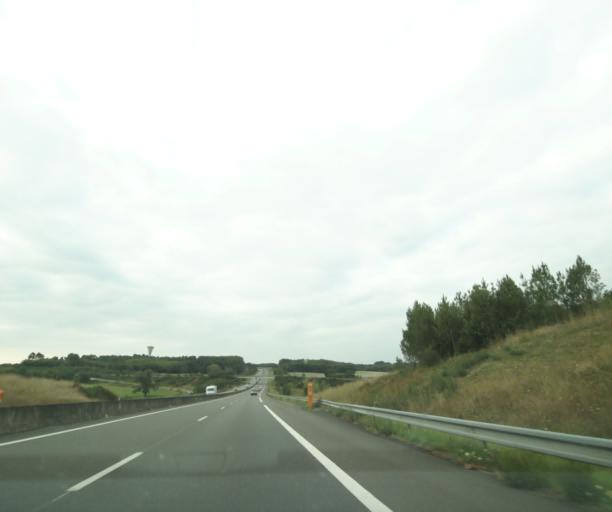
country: FR
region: Pays de la Loire
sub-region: Departement de la Sarthe
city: Luceau
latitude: 47.7102
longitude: 0.3476
